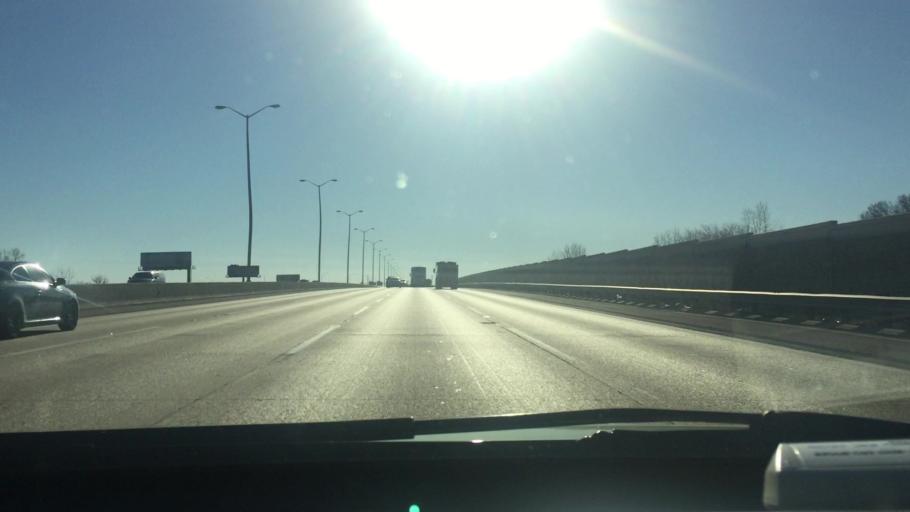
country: US
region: Illinois
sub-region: Lake County
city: Green Oaks
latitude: 42.2874
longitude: -87.9072
